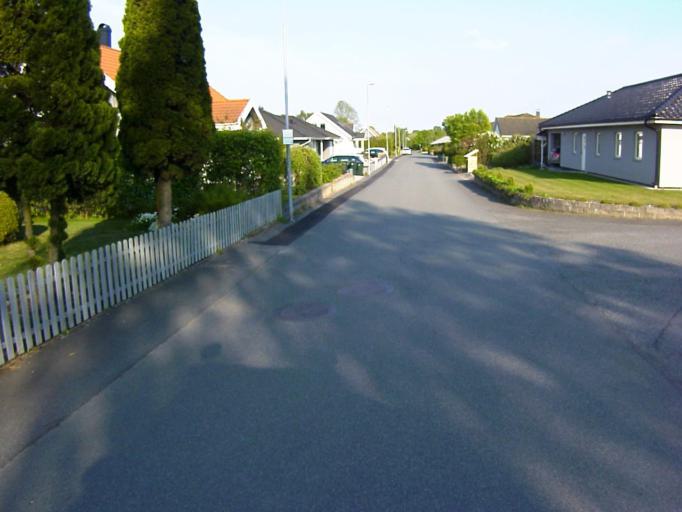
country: SE
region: Skane
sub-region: Kristianstads Kommun
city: Onnestad
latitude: 56.0535
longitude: 14.0159
